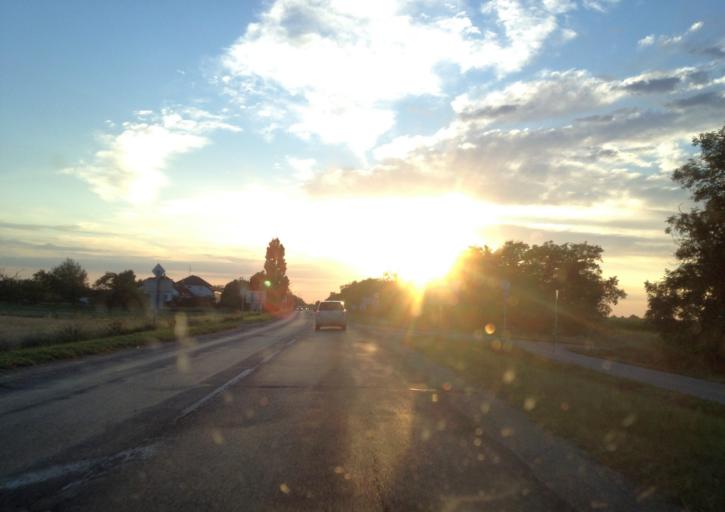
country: HU
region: Gyor-Moson-Sopron
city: Mosonmagyarovar
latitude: 47.8952
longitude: 17.2185
